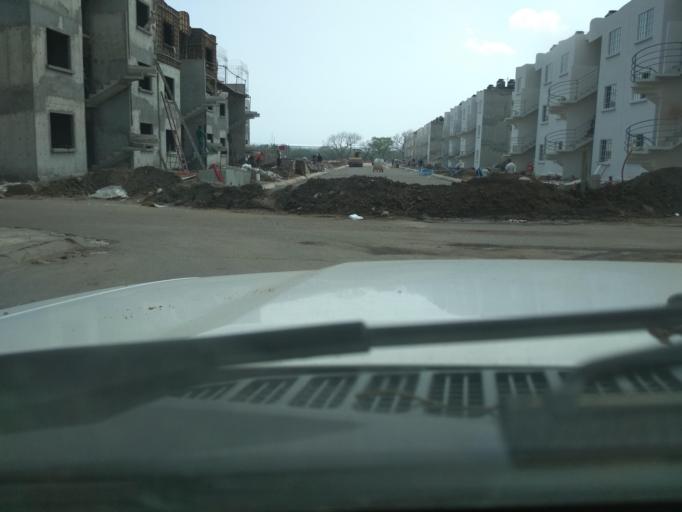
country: MX
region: Veracruz
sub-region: Veracruz
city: Lomas de Rio Medio Cuatro
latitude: 19.1842
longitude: -96.2111
